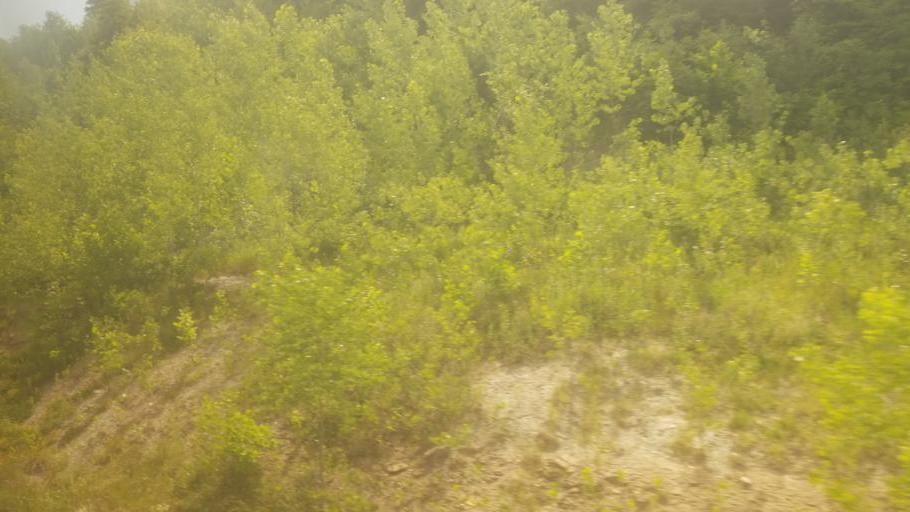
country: US
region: Missouri
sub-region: Jackson County
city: East Independence
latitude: 39.1655
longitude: -94.3586
